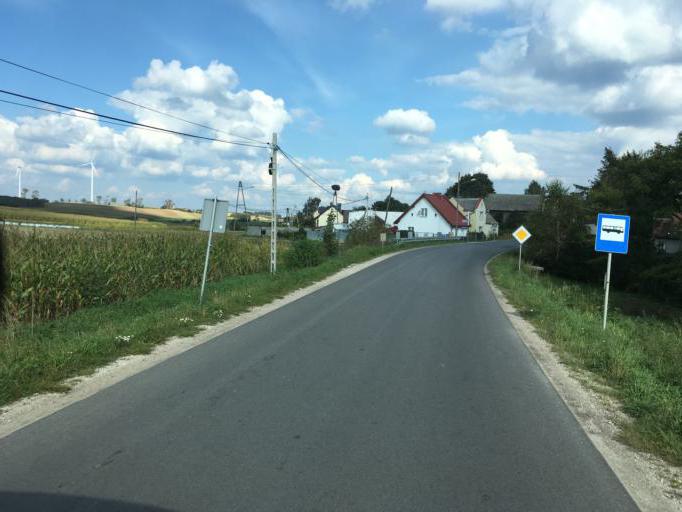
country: PL
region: Kujawsko-Pomorskie
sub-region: Powiat tucholski
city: Tuchola
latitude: 53.5948
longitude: 17.8842
